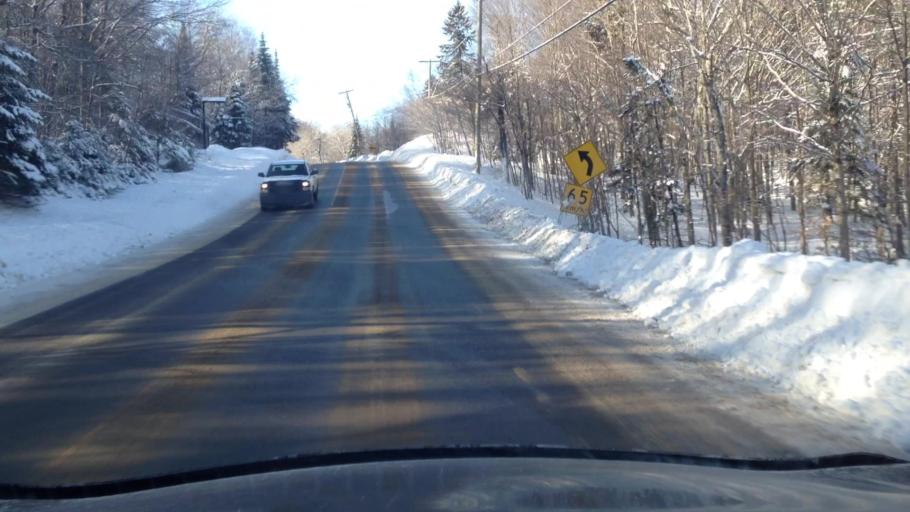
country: CA
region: Quebec
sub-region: Laurentides
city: Sainte-Agathe-des-Monts
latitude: 45.9357
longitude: -74.4394
